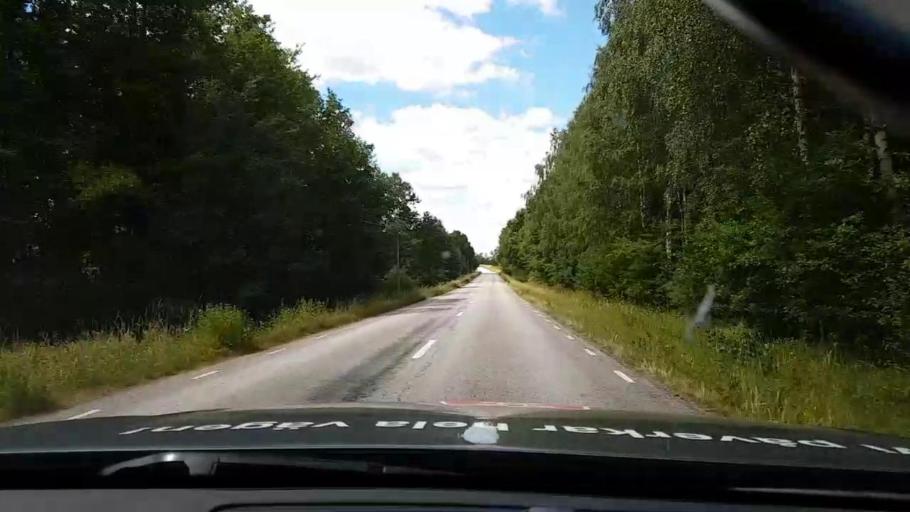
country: SE
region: Kalmar
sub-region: Vasterviks Kommun
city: Forserum
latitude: 58.0392
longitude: 16.4356
